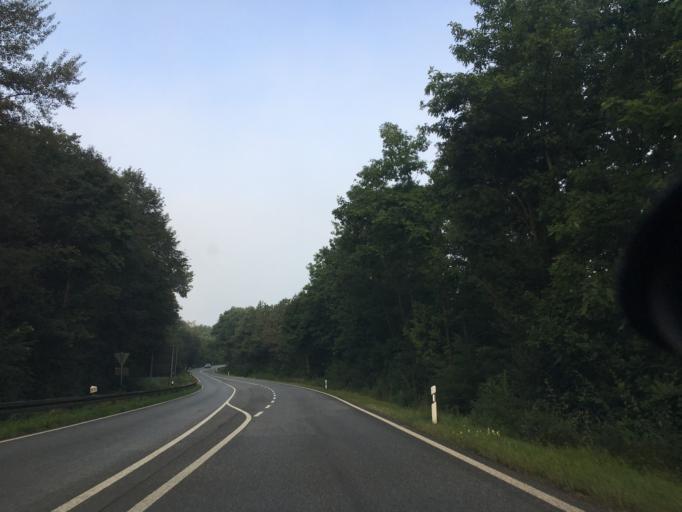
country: DE
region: Hesse
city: Niederrad
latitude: 50.0561
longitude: 8.6453
